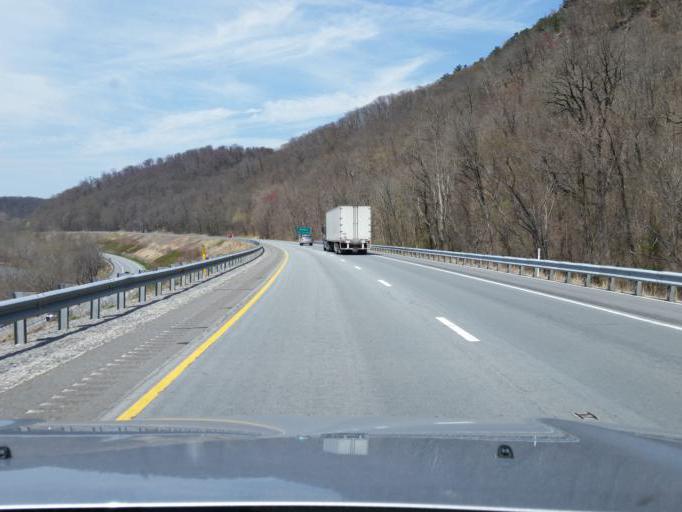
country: US
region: Pennsylvania
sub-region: Perry County
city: Duncannon
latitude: 40.4718
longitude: -77.0321
